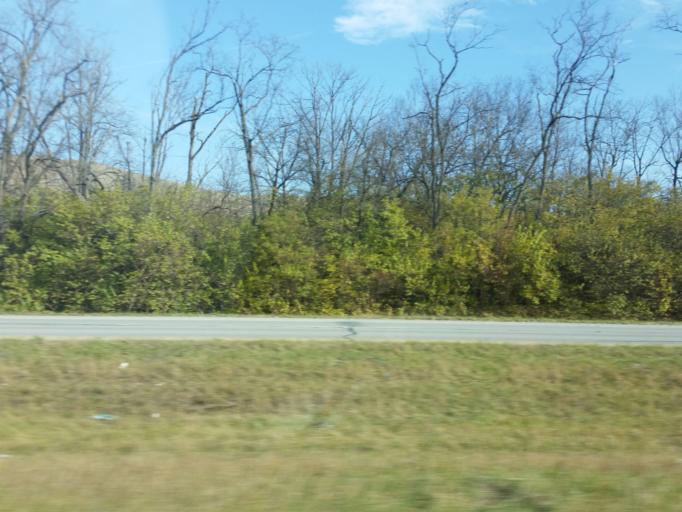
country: US
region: Ohio
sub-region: Hamilton County
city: Dry Ridge
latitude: 39.2728
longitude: -84.6037
